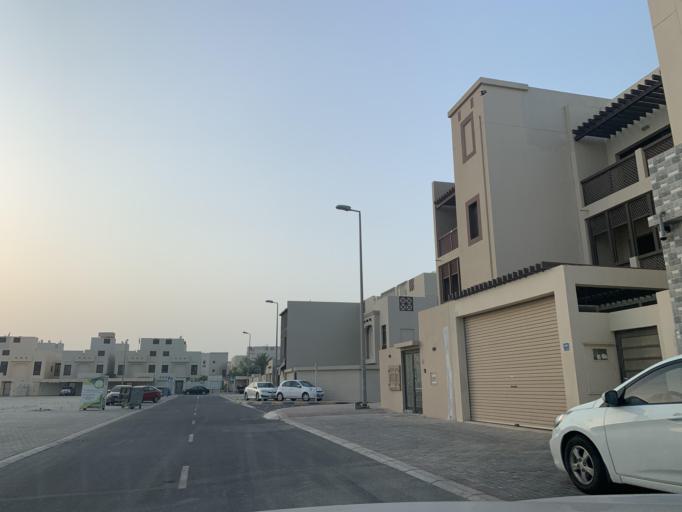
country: BH
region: Manama
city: Jidd Hafs
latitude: 26.2231
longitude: 50.4483
